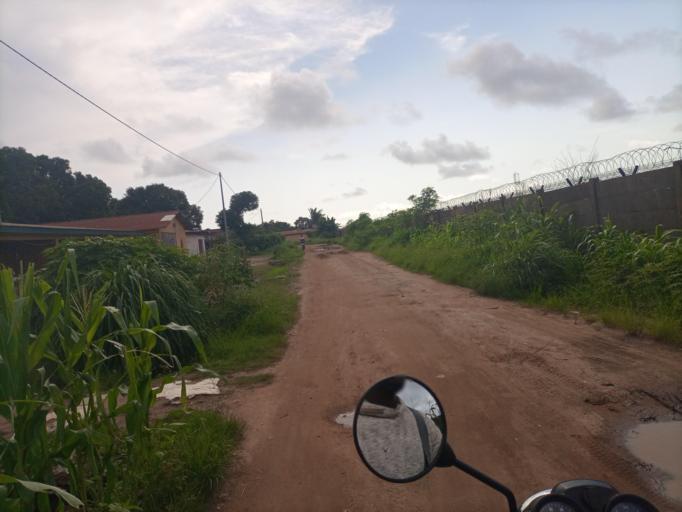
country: SL
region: Northern Province
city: Masoyila
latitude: 8.6106
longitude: -13.1834
